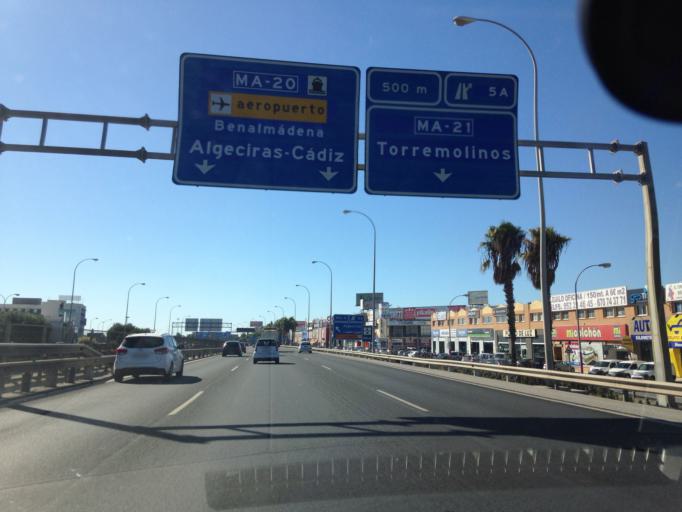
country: ES
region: Andalusia
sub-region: Provincia de Malaga
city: Malaga
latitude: 36.6937
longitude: -4.4606
